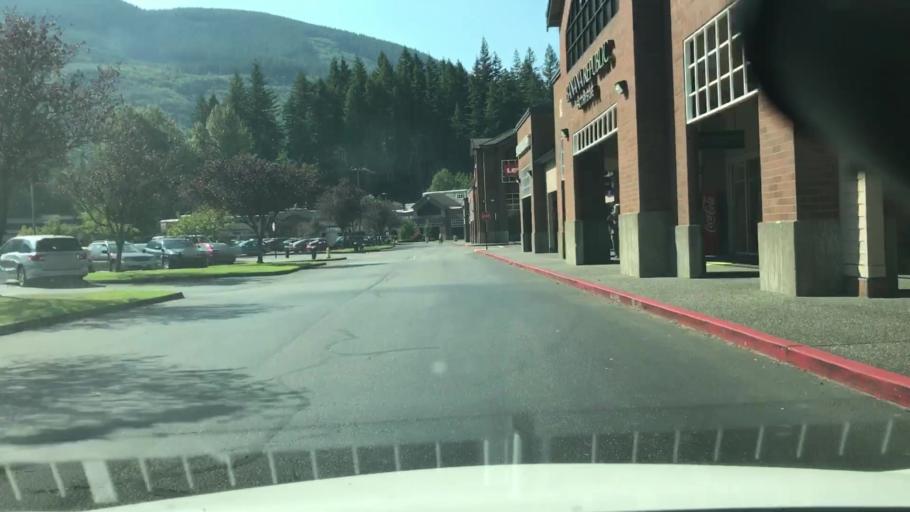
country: US
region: Washington
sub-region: King County
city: North Bend
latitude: 47.4917
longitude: -121.7949
